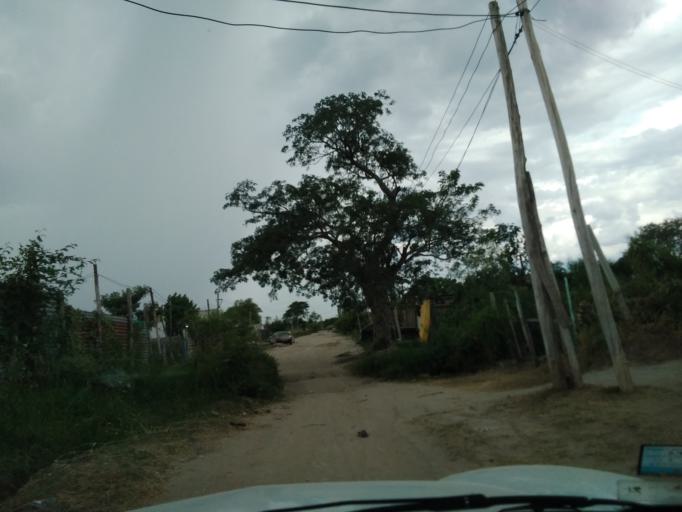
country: AR
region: Corrientes
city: Corrientes
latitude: -27.5229
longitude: -58.7874
